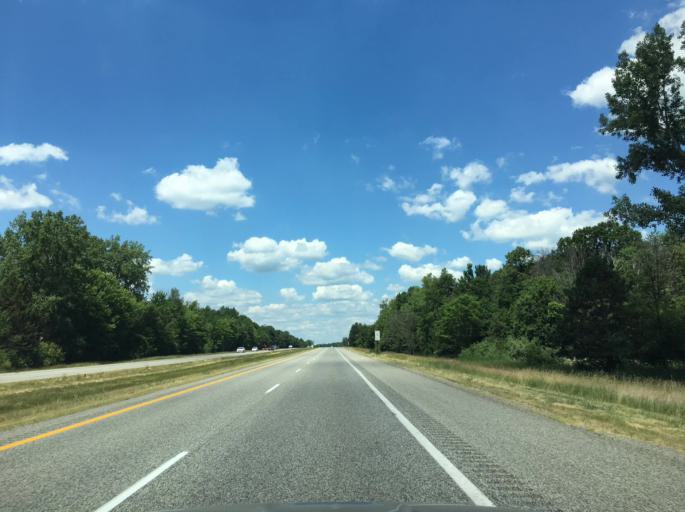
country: US
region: Michigan
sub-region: Midland County
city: Midland
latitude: 43.6476
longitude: -84.1944
